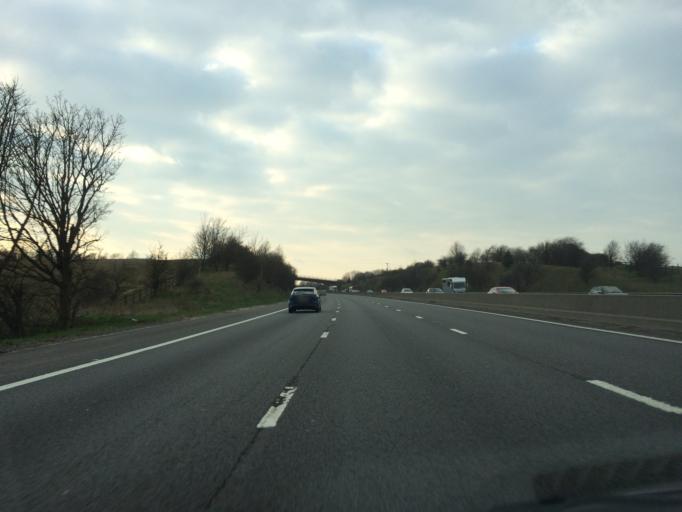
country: GB
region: England
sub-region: Wiltshire
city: Aldbourne
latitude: 51.5034
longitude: -1.5913
